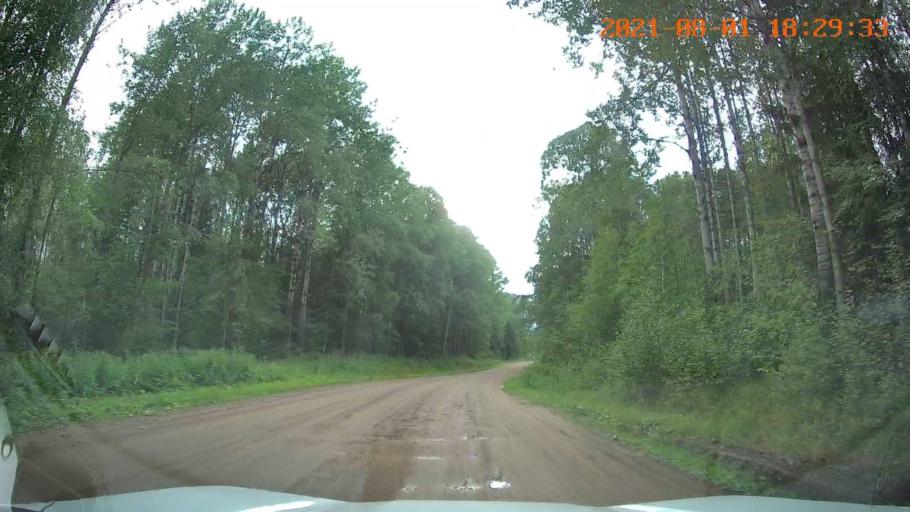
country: RU
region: Leningrad
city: Voznesen'ye
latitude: 60.8856
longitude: 35.3733
